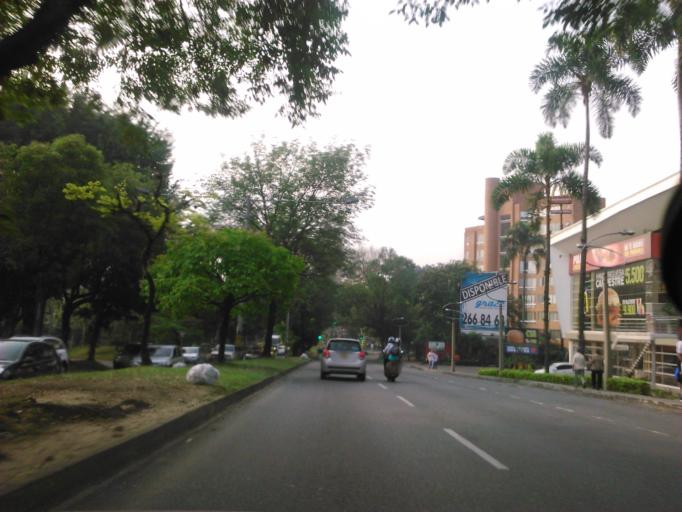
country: CO
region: Antioquia
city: Itagui
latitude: 6.2174
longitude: -75.5983
